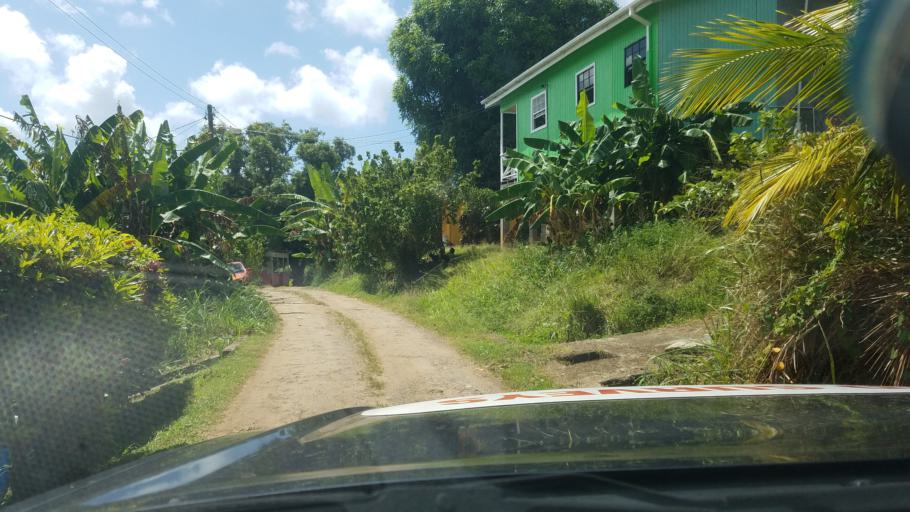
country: LC
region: Castries Quarter
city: Bisee
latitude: 14.0295
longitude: -60.9525
